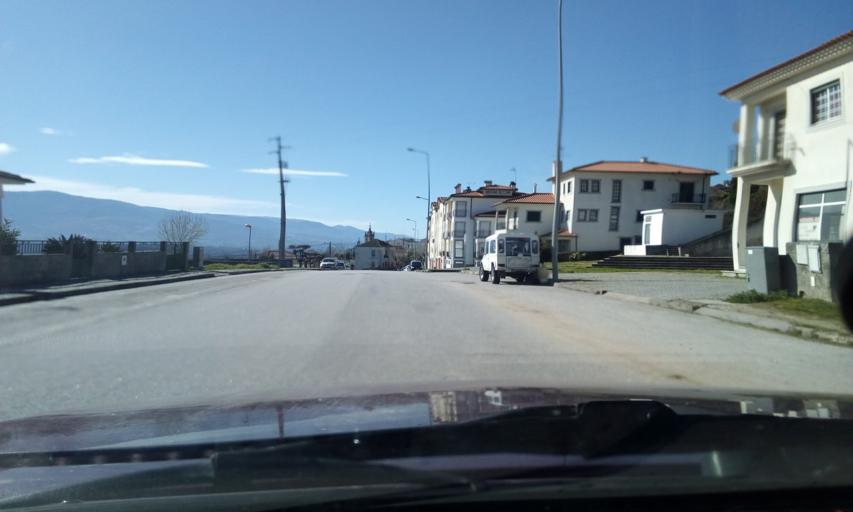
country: PT
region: Guarda
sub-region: Fornos de Algodres
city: Fornos de Algodres
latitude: 40.6243
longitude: -7.5346
